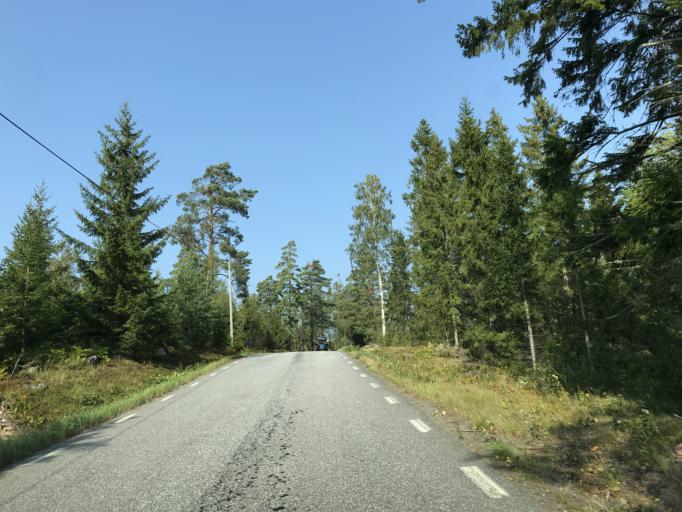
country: SE
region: Stockholm
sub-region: Norrtalje Kommun
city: Bjorko
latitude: 59.8654
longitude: 19.0469
